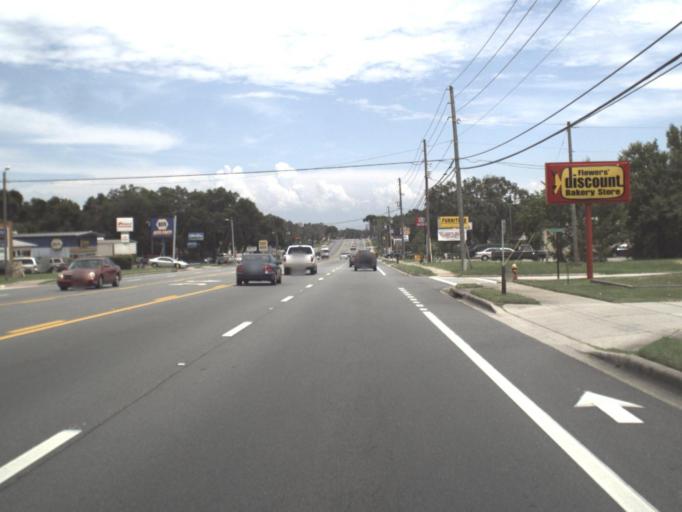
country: US
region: Florida
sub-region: Citrus County
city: Inverness Highlands North
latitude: 28.8414
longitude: -82.3619
